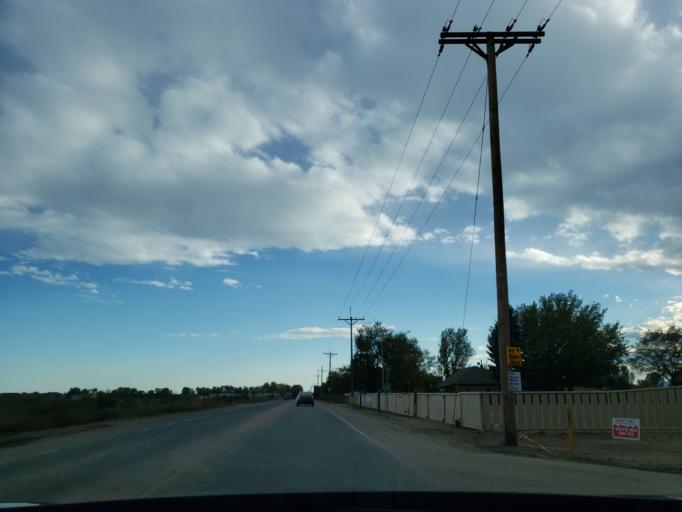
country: US
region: Colorado
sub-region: Larimer County
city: Fort Collins
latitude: 40.5959
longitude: -105.0294
